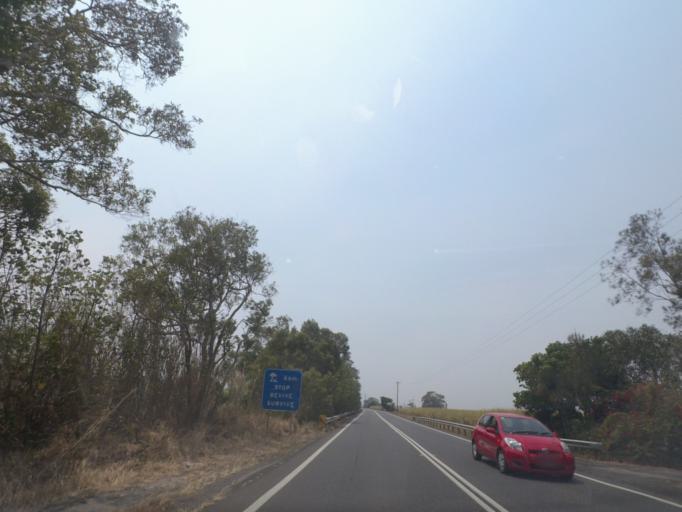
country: AU
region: New South Wales
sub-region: Richmond Valley
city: Evans Head
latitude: -28.9833
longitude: 153.4621
